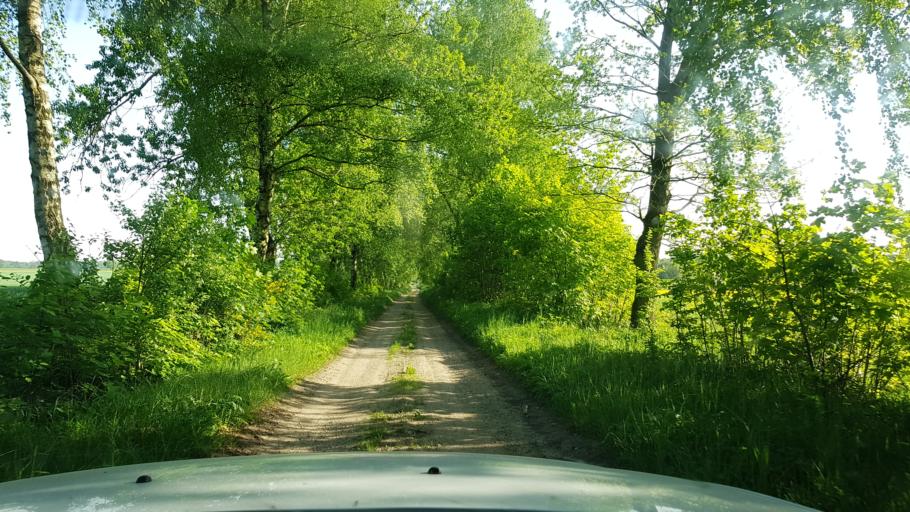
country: PL
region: West Pomeranian Voivodeship
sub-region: Powiat lobeski
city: Resko
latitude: 53.7009
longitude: 15.3368
